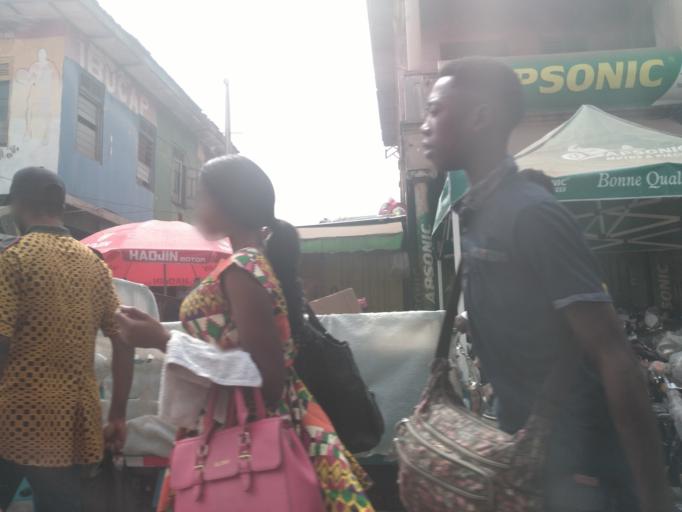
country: GH
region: Ashanti
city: Kumasi
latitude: 6.6995
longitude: -1.6172
